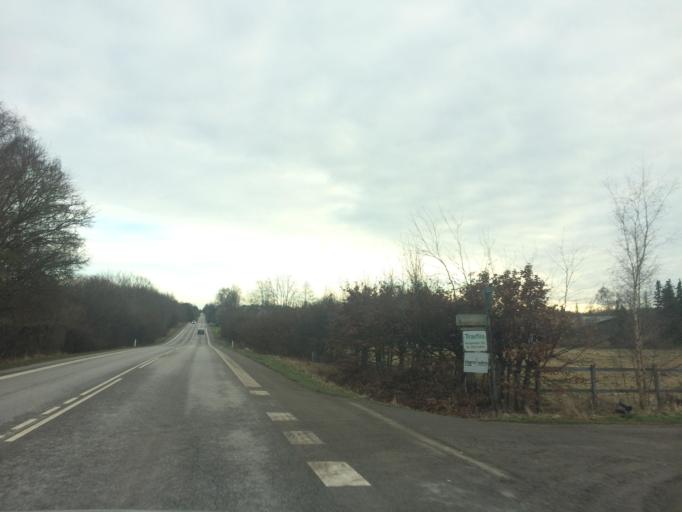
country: DK
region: Capital Region
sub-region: Fredensborg Kommune
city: Fredensborg
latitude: 55.9351
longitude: 12.4348
